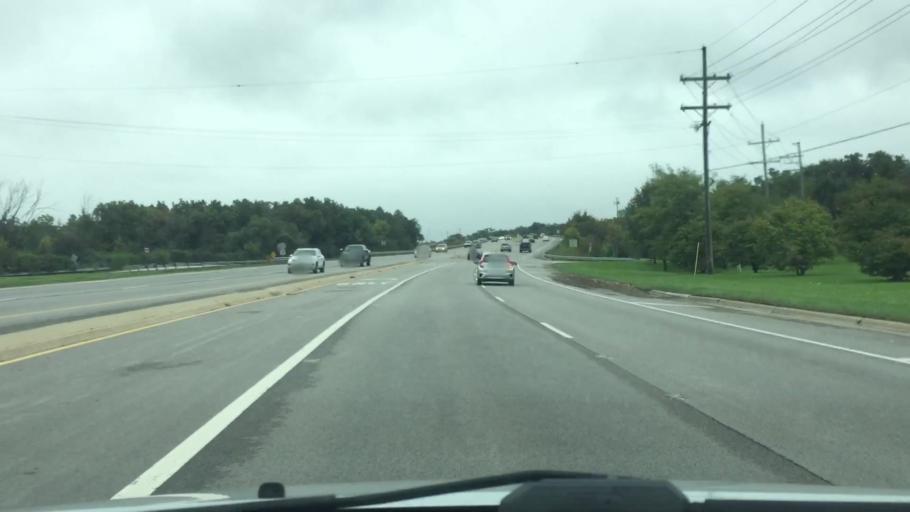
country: US
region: Illinois
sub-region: McHenry County
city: Crystal Lake
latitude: 42.2352
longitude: -88.2868
